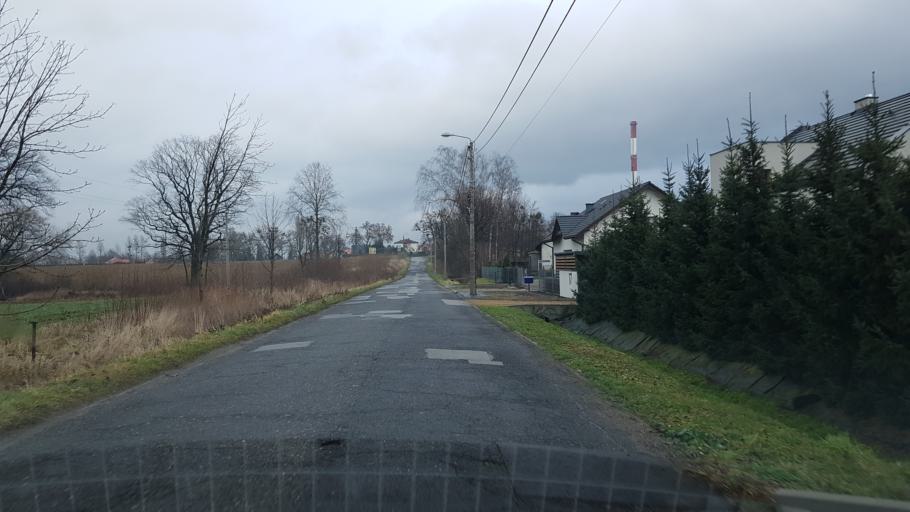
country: PL
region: Silesian Voivodeship
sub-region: Powiat pszczynski
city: Pszczyna
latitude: 49.9662
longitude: 18.9157
